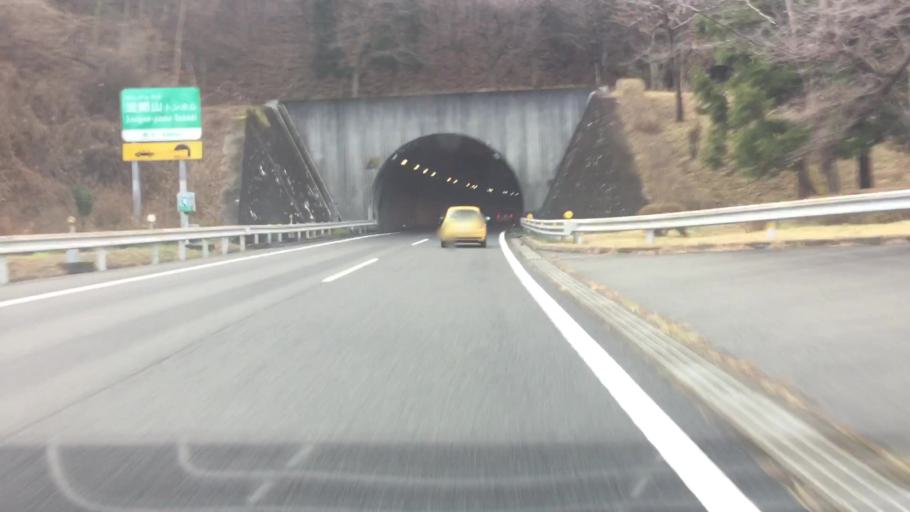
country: JP
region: Gunma
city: Annaka
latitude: 36.3348
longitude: 138.7113
